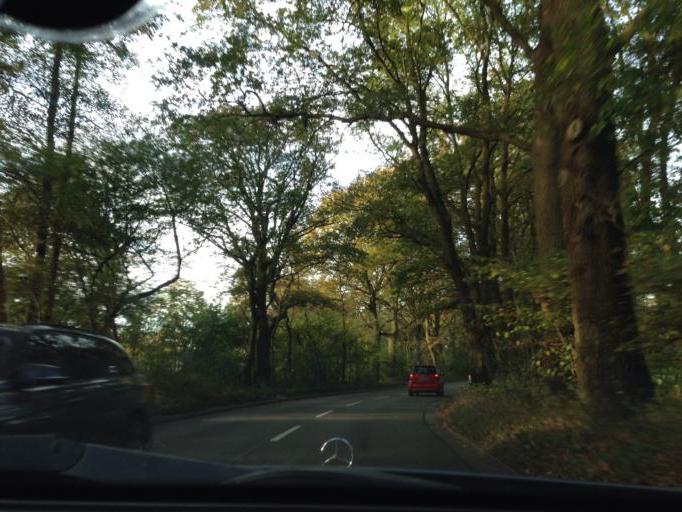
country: DE
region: Hamburg
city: Sasel
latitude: 53.6397
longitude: 10.1289
